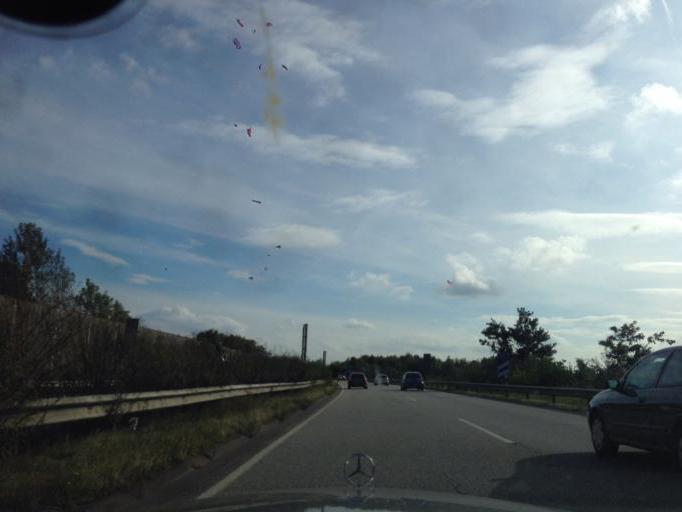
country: DE
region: Schleswig-Holstein
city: Hogersdorf
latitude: 53.9218
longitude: 10.2737
